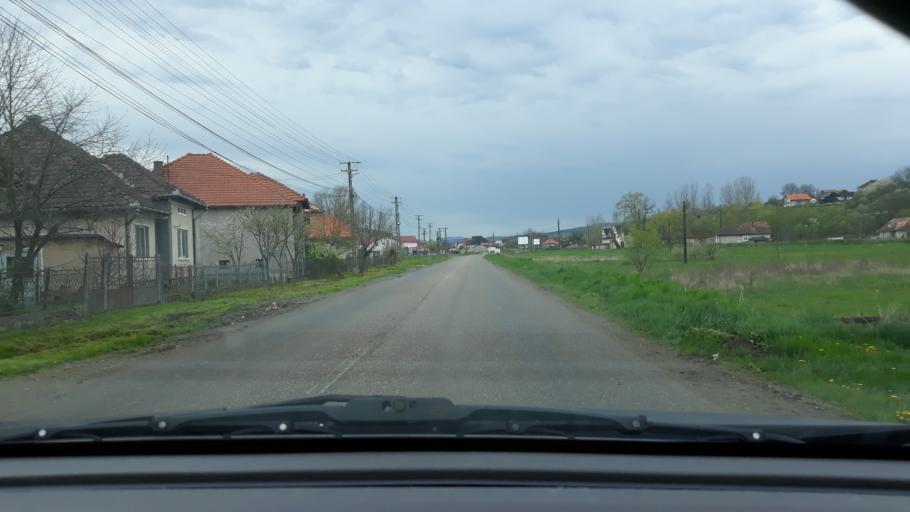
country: RO
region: Salaj
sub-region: Comuna Salatig
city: Salatig
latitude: 47.3686
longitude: 23.1453
